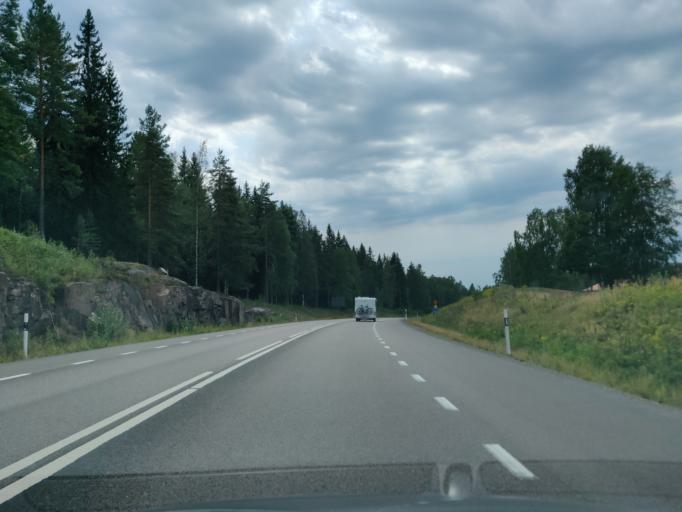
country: SE
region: Vaermland
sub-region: Munkfors Kommun
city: Munkfors
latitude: 59.8329
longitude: 13.5458
